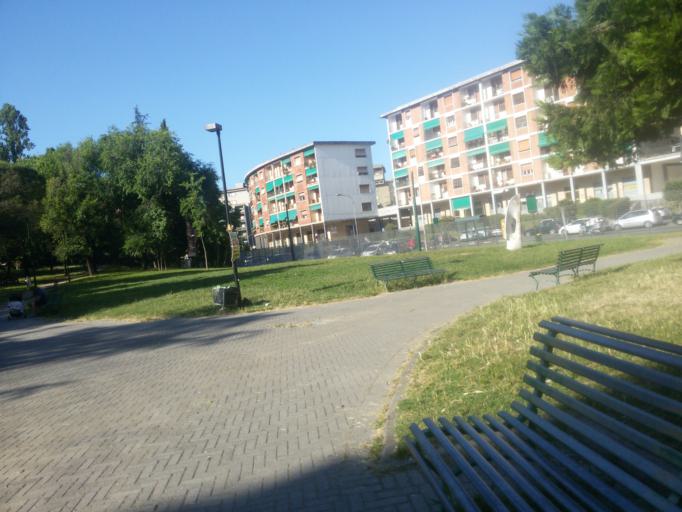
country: IT
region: Liguria
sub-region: Provincia di La Spezia
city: La Spezia
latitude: 44.1188
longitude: 9.8404
